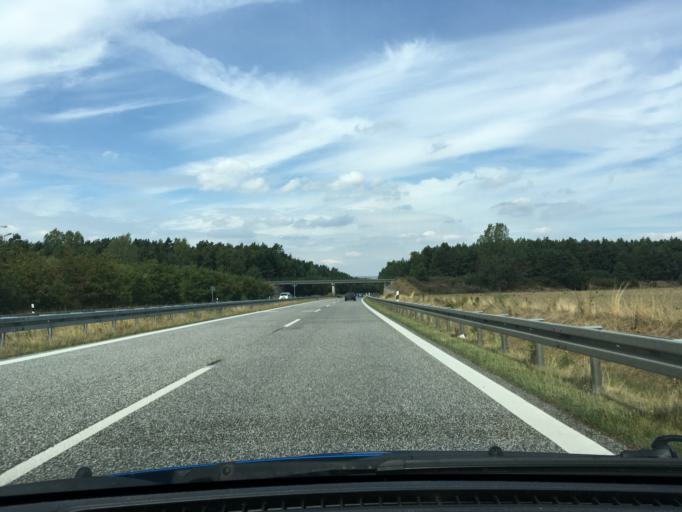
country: DE
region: Mecklenburg-Vorpommern
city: Mirow
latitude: 53.4929
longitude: 11.4791
